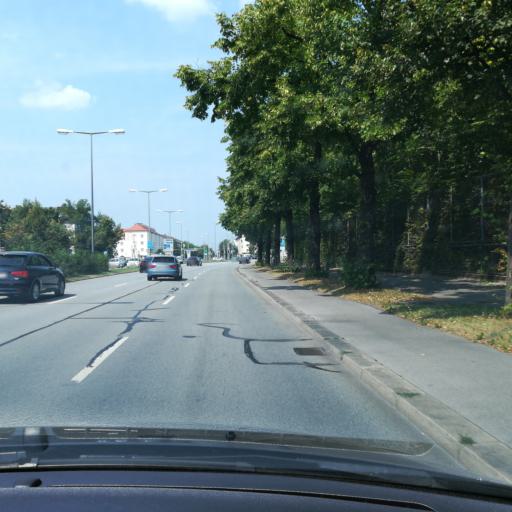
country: DE
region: Bavaria
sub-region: Upper Bavaria
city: Neuried
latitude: 48.1240
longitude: 11.5028
